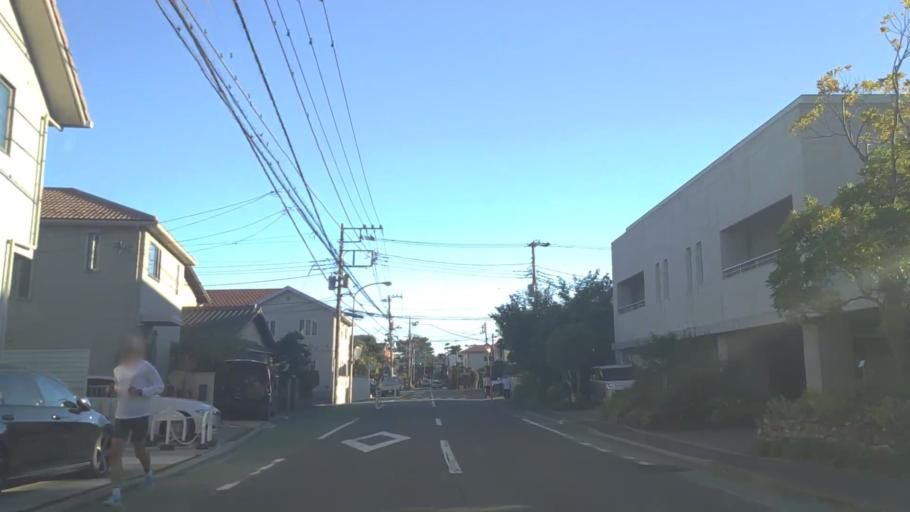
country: JP
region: Kanagawa
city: Chigasaki
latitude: 35.3240
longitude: 139.4151
